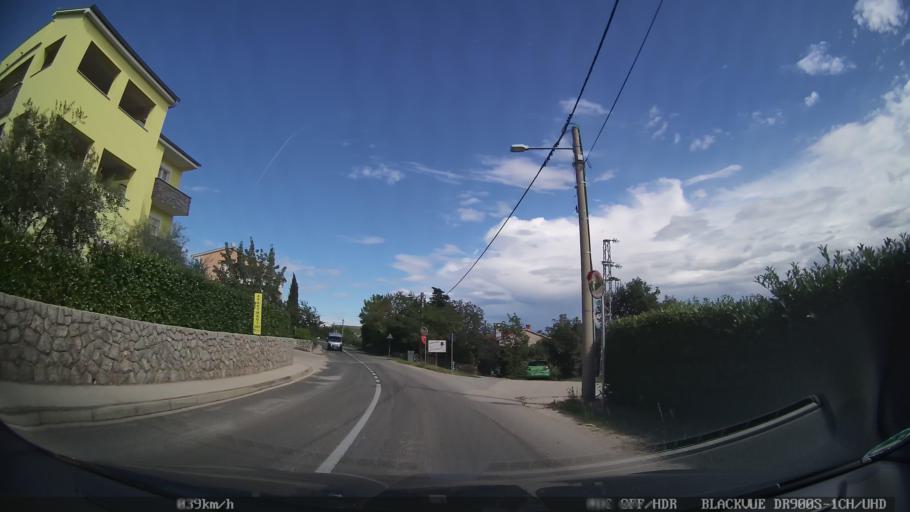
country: HR
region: Primorsko-Goranska
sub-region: Grad Krk
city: Krk
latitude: 45.0436
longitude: 14.5432
